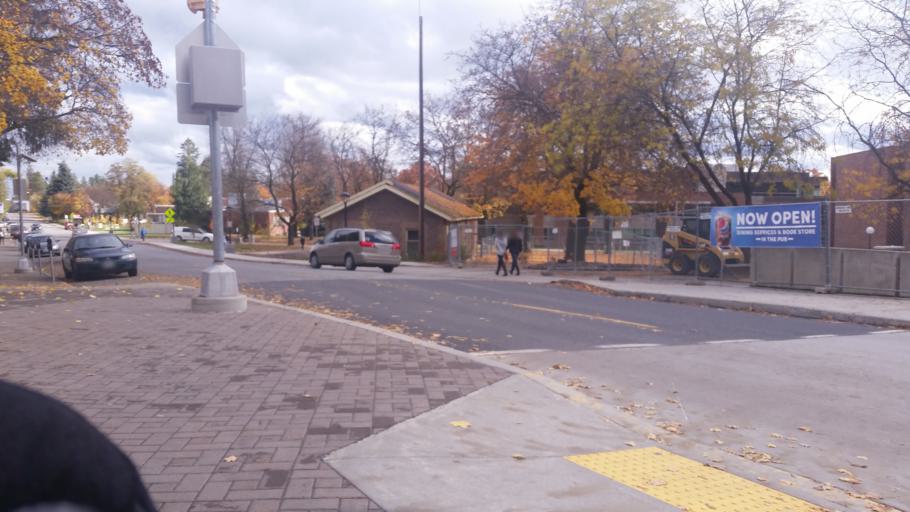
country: US
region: Washington
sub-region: Spokane County
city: Cheney
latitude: 47.4928
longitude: -117.5835
